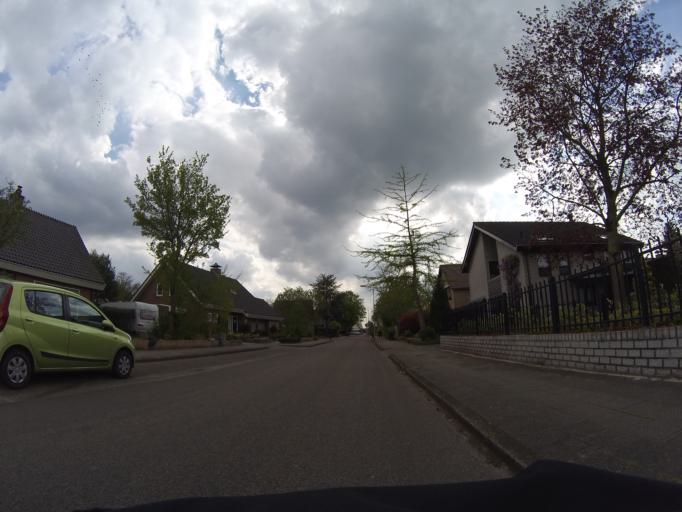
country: NL
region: Gelderland
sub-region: Gemeente Hattem
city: Hattem
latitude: 52.4657
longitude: 6.0027
